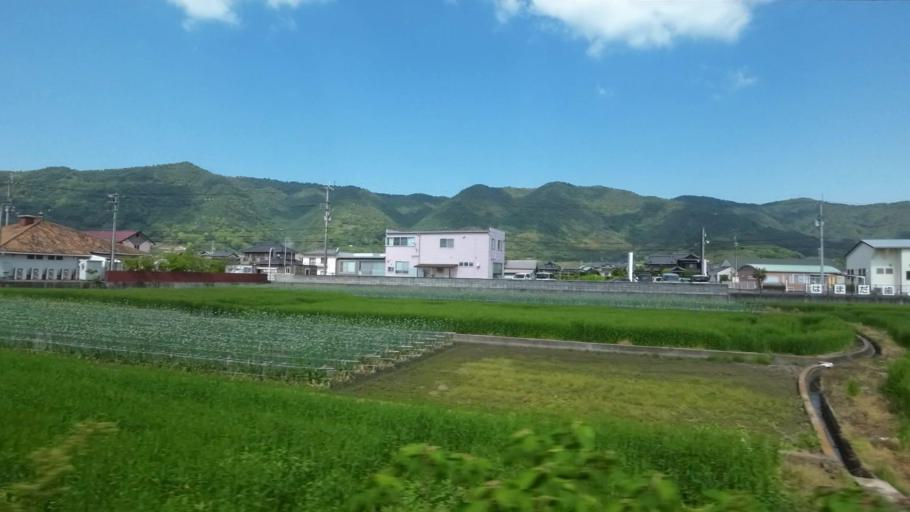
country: JP
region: Kagawa
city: Kan'onjicho
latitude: 34.1654
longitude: 133.6900
